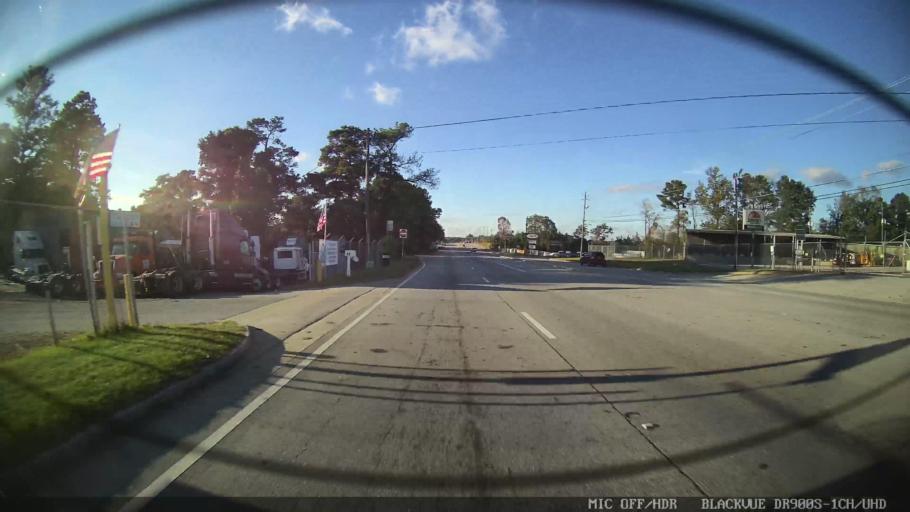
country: US
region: Georgia
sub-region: Clayton County
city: Conley
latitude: 33.6337
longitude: -84.3171
